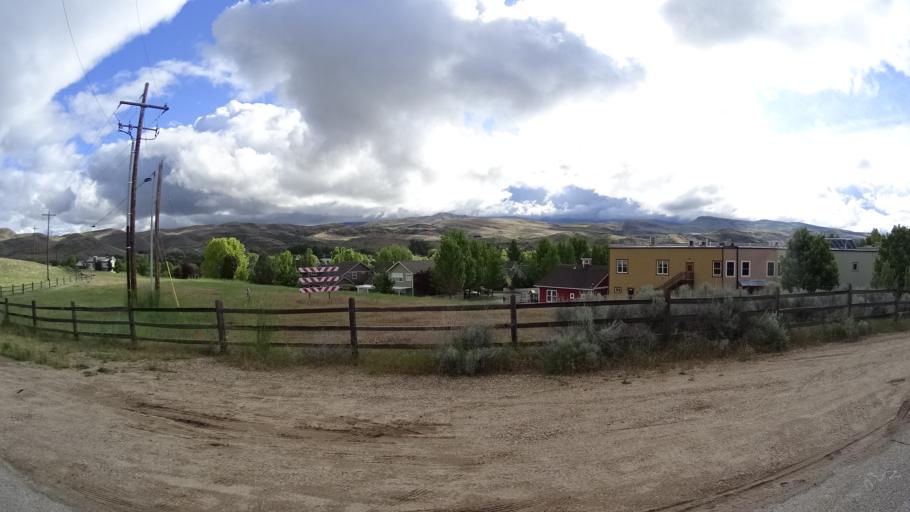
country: US
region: Idaho
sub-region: Ada County
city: Eagle
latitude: 43.7255
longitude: -116.2633
